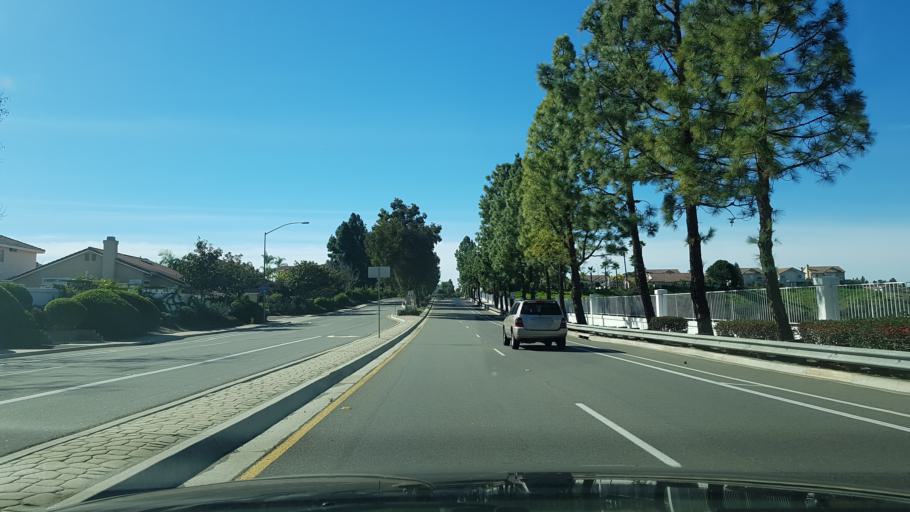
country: US
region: California
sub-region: San Diego County
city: Fairbanks Ranch
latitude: 32.9304
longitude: -117.1509
